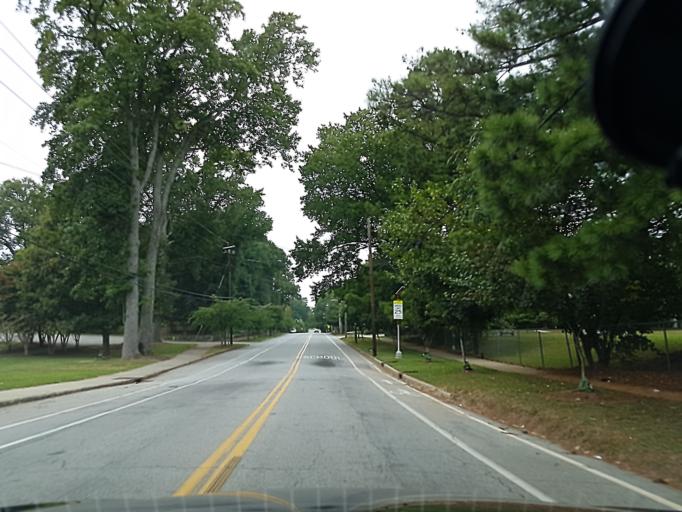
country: US
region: Georgia
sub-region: DeKalb County
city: Druid Hills
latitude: 33.7534
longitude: -84.3355
